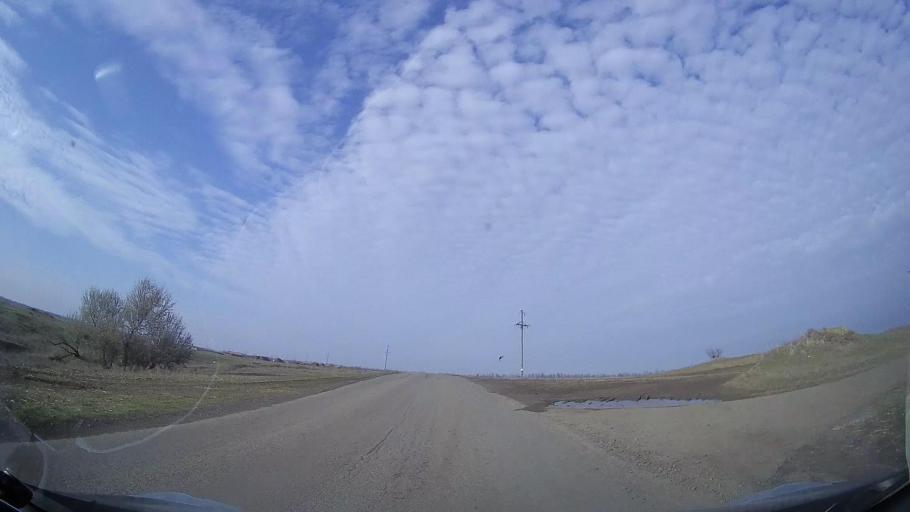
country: RU
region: Rostov
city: Gigant
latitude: 46.8453
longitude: 41.3293
